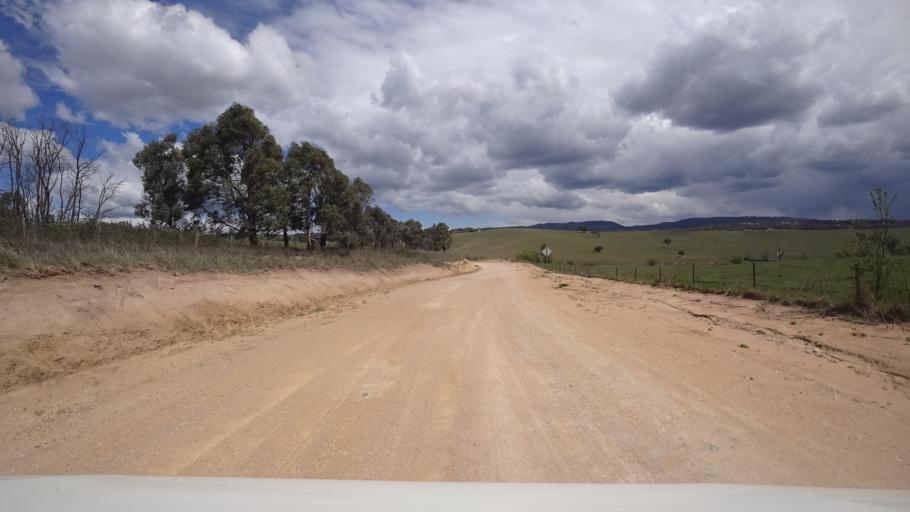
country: AU
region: New South Wales
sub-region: Oberon
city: Oberon
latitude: -33.5762
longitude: 149.8971
